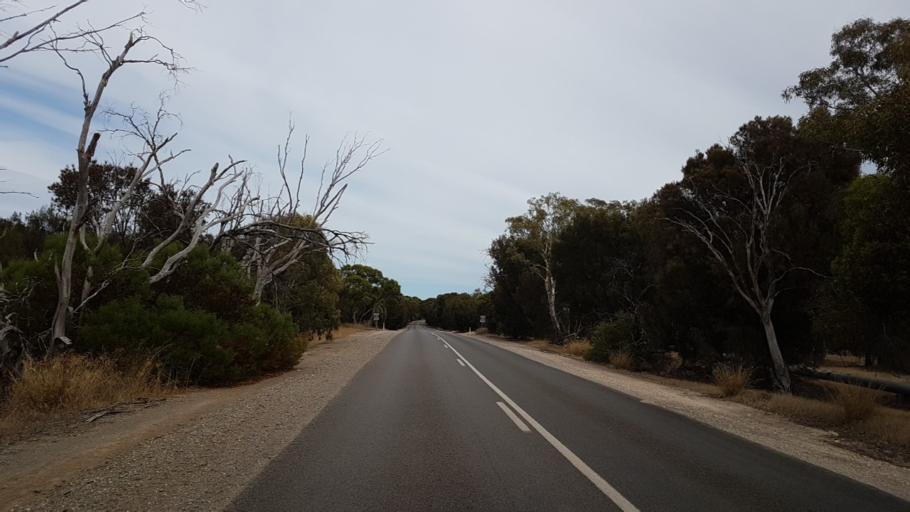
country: AU
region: South Australia
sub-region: Yorke Peninsula
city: Port Victoria
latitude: -34.7731
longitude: 137.6057
